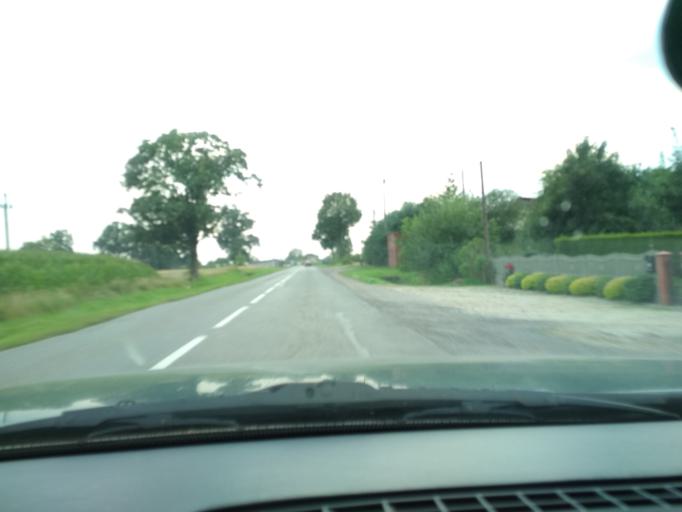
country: PL
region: Silesian Voivodeship
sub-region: Powiat cieszynski
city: Chybie
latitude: 49.9446
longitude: 18.8273
